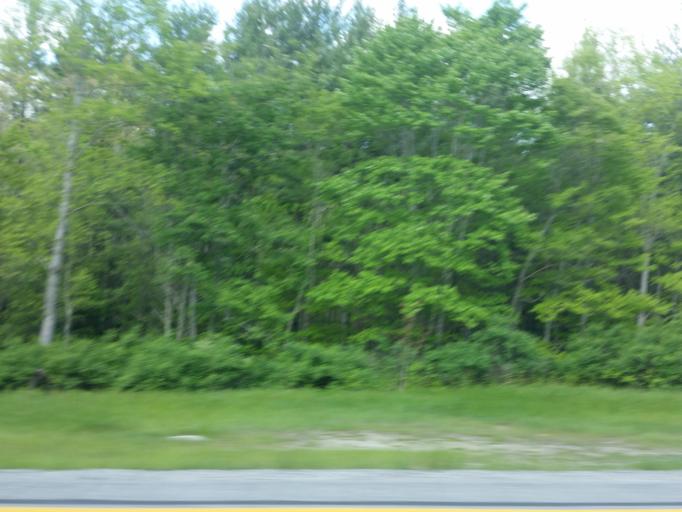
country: US
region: West Virginia
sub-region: Raleigh County
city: Beaver
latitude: 37.7056
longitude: -81.1512
